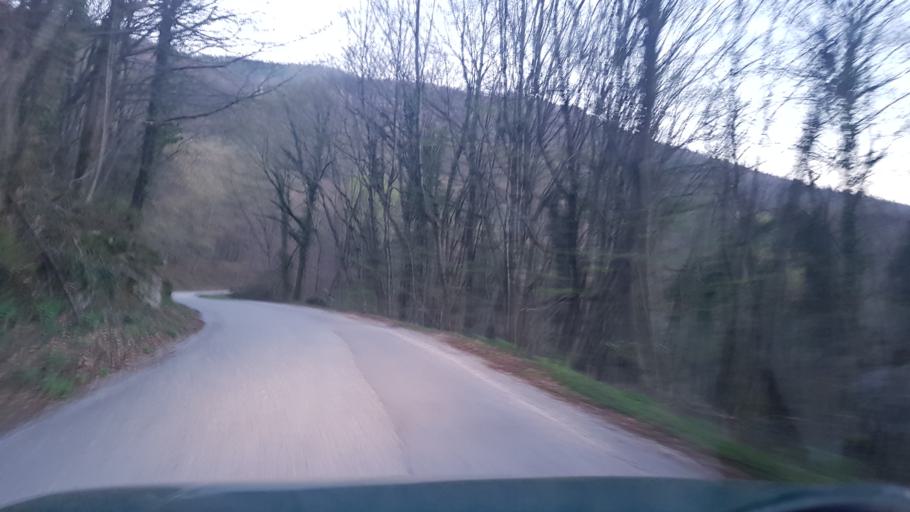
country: SI
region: Kanal
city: Kanal
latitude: 46.0808
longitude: 13.6448
